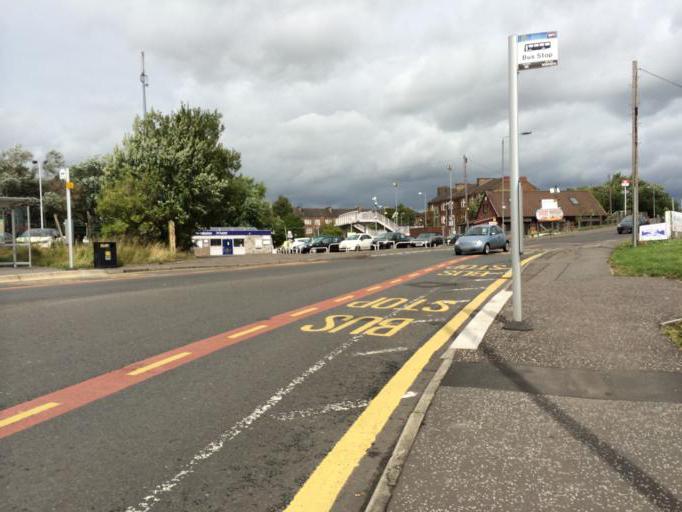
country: GB
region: Scotland
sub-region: North Lanarkshire
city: Stepps
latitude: 55.8528
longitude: -4.1600
